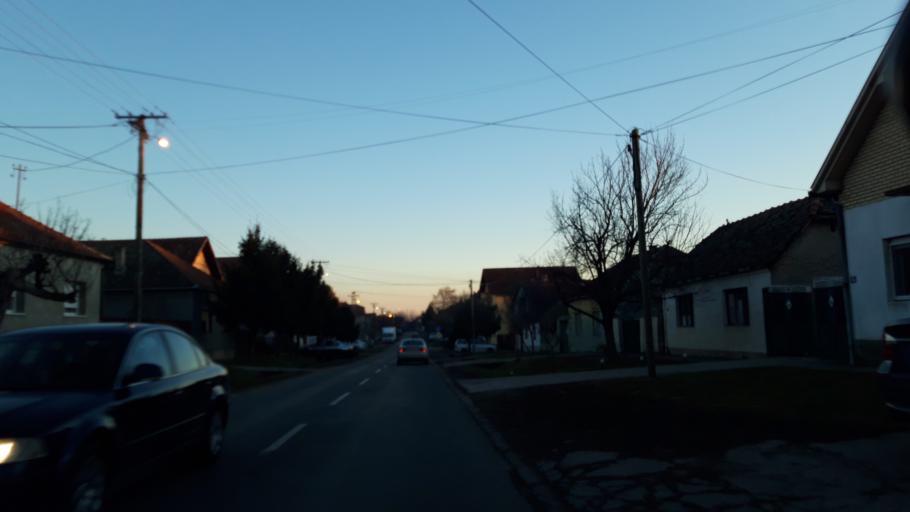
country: RS
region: Autonomna Pokrajina Vojvodina
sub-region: Sremski Okrug
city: Ingija
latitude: 45.0406
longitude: 20.0788
